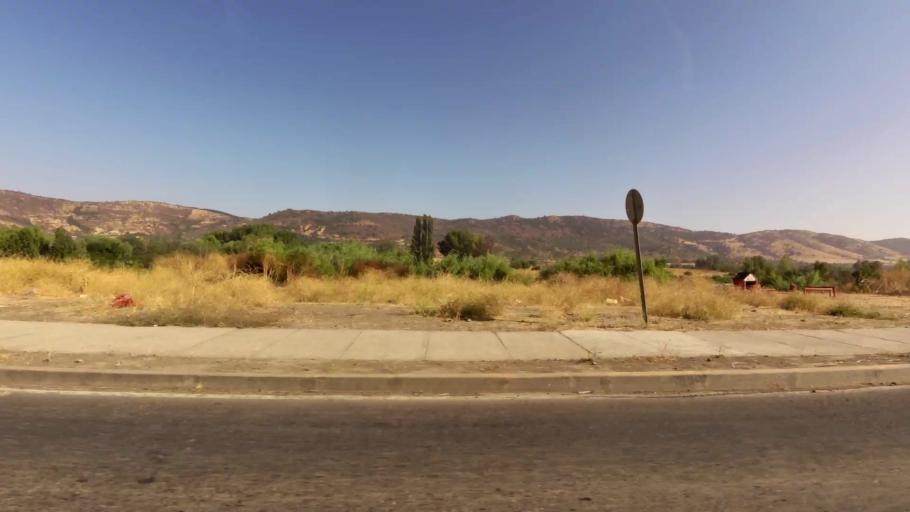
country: CL
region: Maule
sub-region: Provincia de Talca
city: Talca
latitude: -35.4012
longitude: -71.6594
